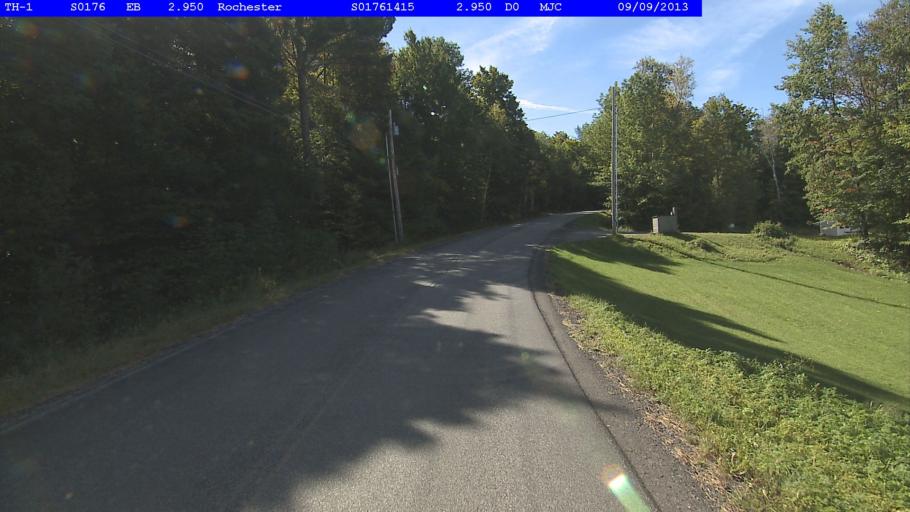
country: US
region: Vermont
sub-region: Orange County
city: Randolph
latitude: 43.8622
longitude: -72.7619
